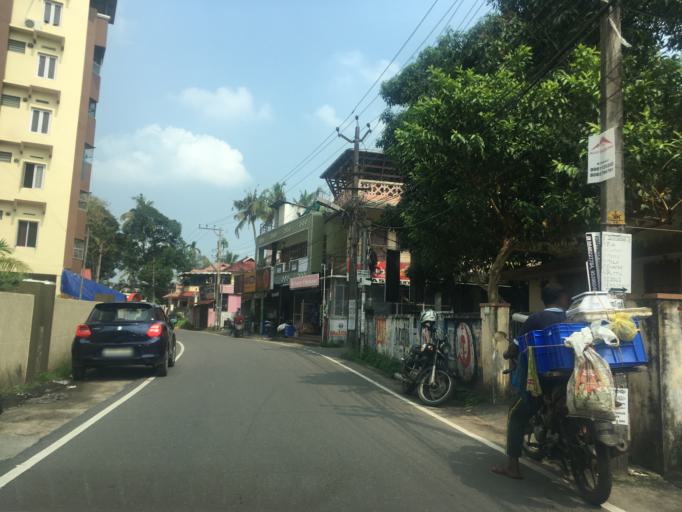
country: IN
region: Kerala
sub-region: Ernakulam
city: Elur
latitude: 10.0347
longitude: 76.3084
